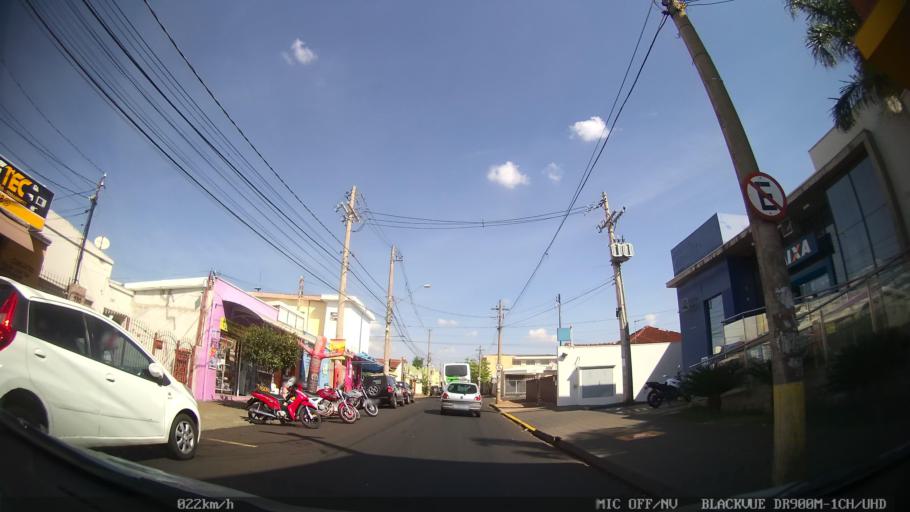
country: BR
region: Sao Paulo
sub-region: Ribeirao Preto
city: Ribeirao Preto
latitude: -21.1844
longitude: -47.8259
